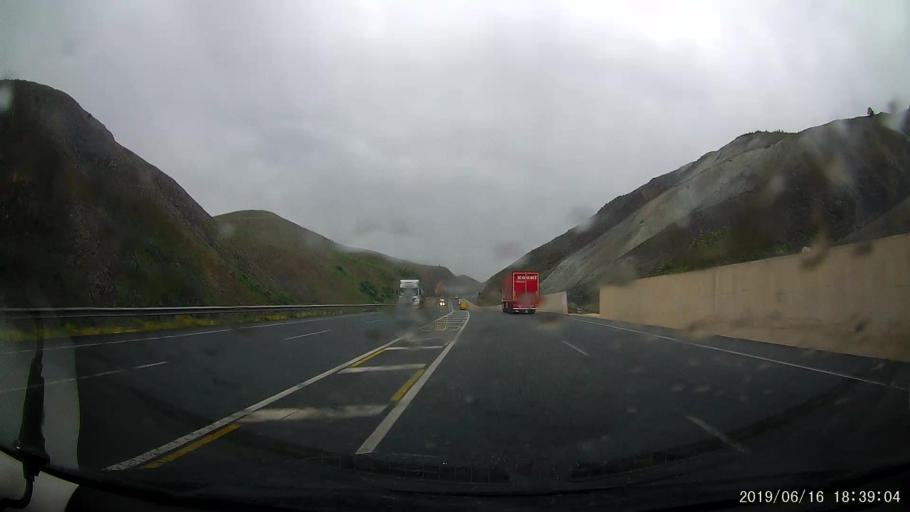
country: TR
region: Erzincan
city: Catalarmut
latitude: 39.8828
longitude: 39.1727
